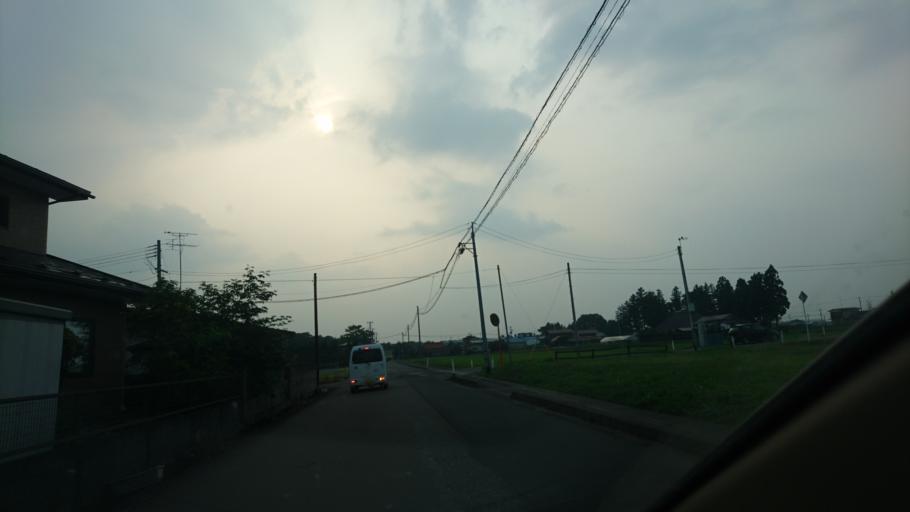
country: JP
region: Iwate
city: Mizusawa
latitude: 39.1698
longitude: 141.1631
